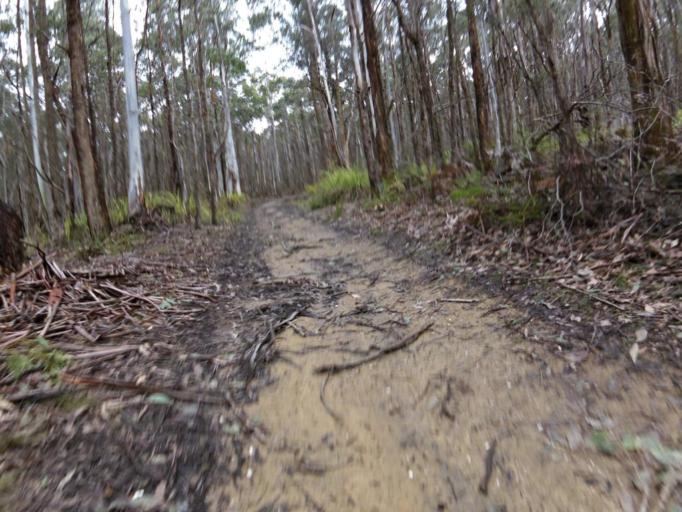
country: AU
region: Victoria
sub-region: Moorabool
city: Bacchus Marsh
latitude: -37.4242
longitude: 144.4696
